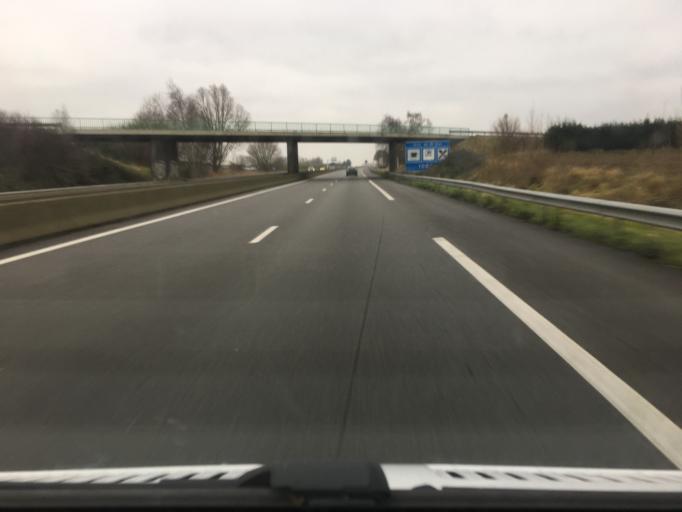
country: FR
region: Nord-Pas-de-Calais
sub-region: Departement du Nord
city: Winnezeele
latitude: 50.8401
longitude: 2.5697
